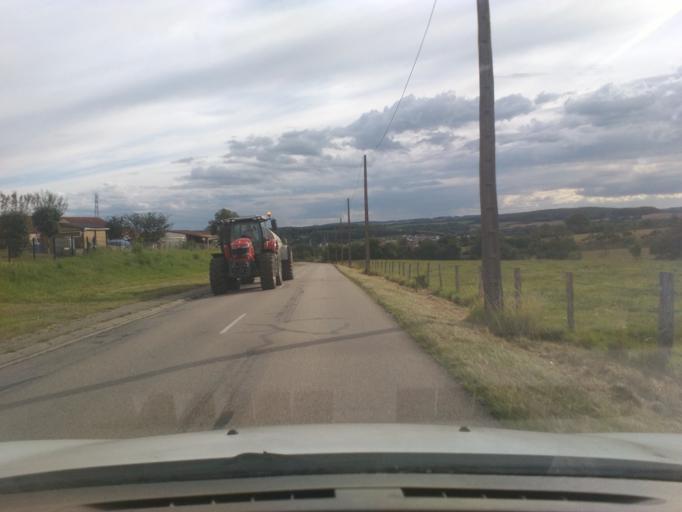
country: FR
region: Lorraine
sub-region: Departement des Vosges
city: Chatel-sur-Moselle
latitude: 48.3191
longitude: 6.4011
